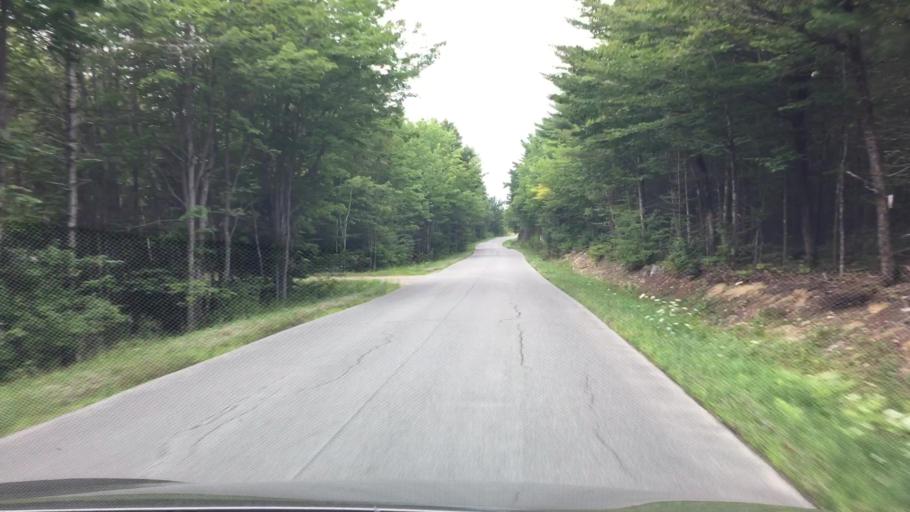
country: US
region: Maine
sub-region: Waldo County
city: Stockton Springs
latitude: 44.5196
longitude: -68.8785
